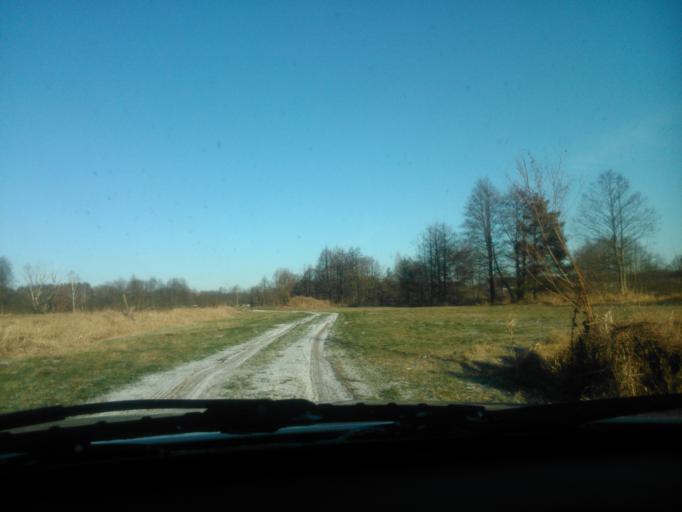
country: PL
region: Warmian-Masurian Voivodeship
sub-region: Powiat nowomiejski
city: Kurzetnik
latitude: 53.3657
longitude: 19.5247
